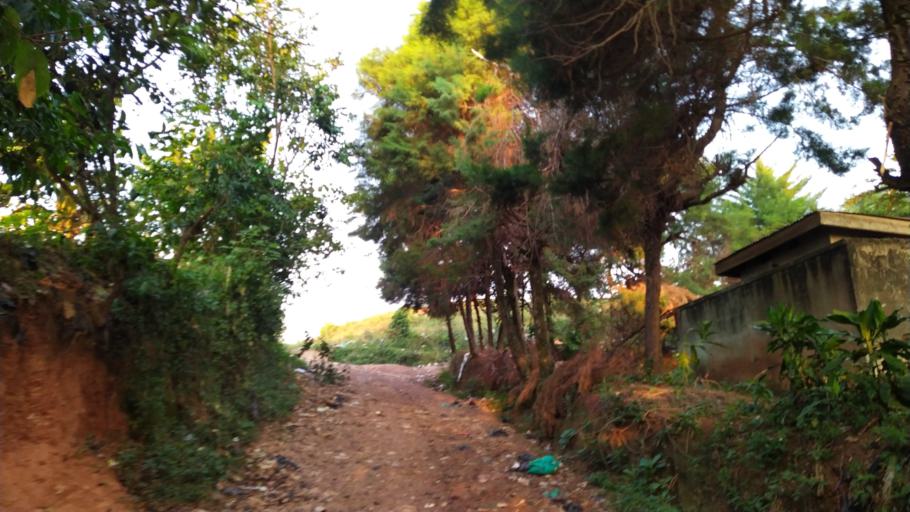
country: UG
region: Central Region
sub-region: Kampala District
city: Kampala
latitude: 0.2699
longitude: 32.5734
